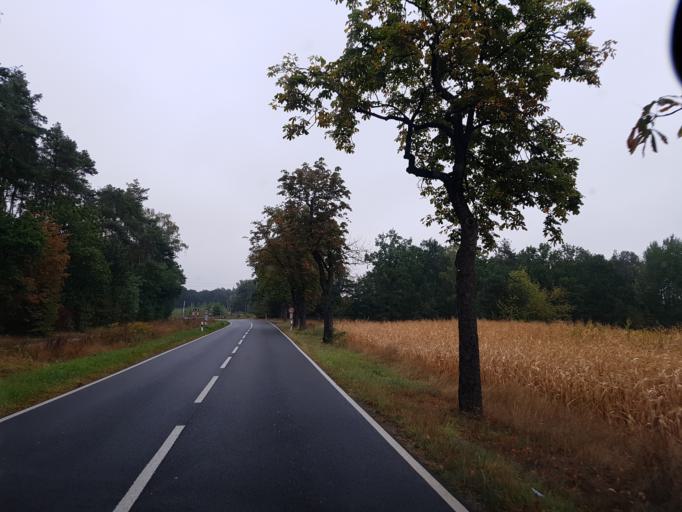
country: DE
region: Brandenburg
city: Hohenleipisch
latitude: 51.4729
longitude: 13.5473
